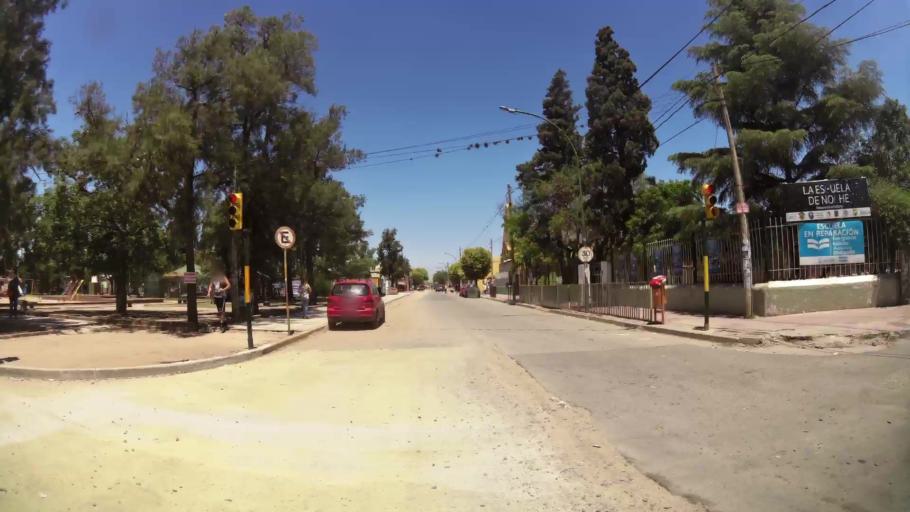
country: AR
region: Cordoba
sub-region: Departamento de Capital
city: Cordoba
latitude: -31.3845
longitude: -64.1340
